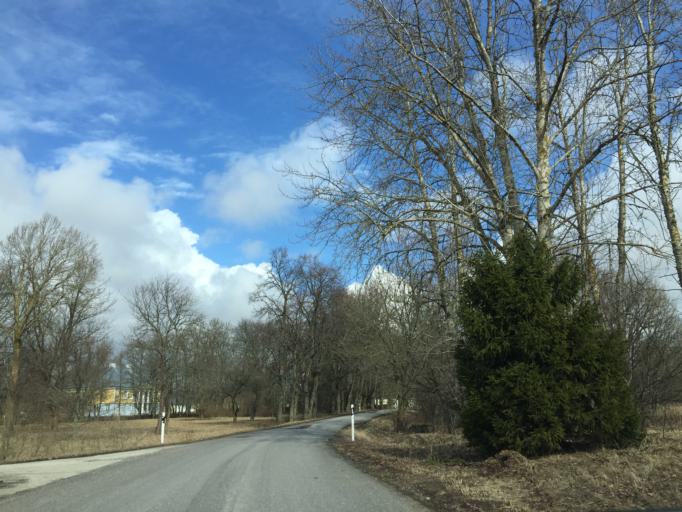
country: EE
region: Laeaene
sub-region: Lihula vald
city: Lihula
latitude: 58.7127
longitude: 23.8151
